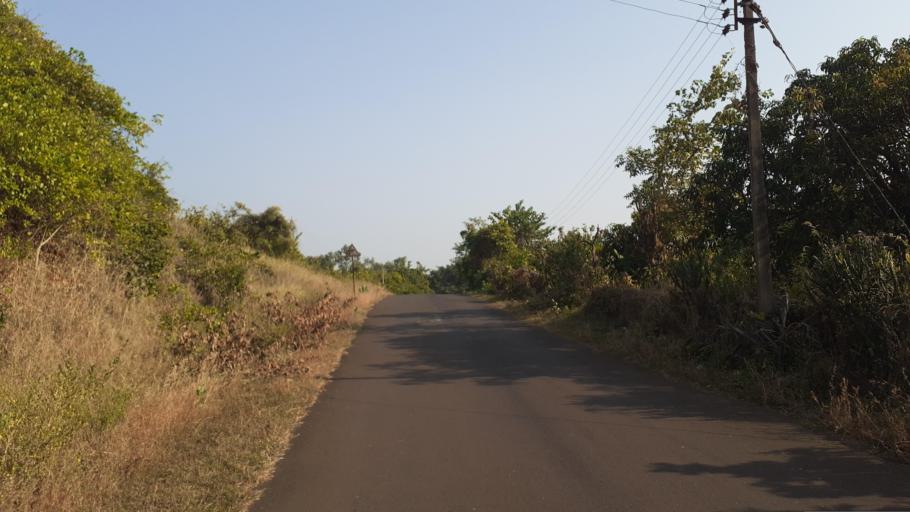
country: IN
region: Maharashtra
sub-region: Ratnagiri
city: Ratnagiri
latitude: 17.2192
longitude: 73.2467
